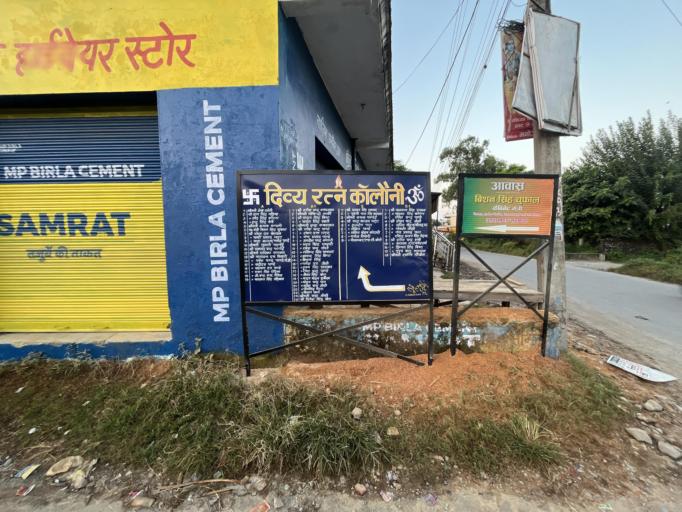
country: IN
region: Uttarakhand
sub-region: Naini Tal
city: Haldwani
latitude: 29.2068
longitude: 79.4863
